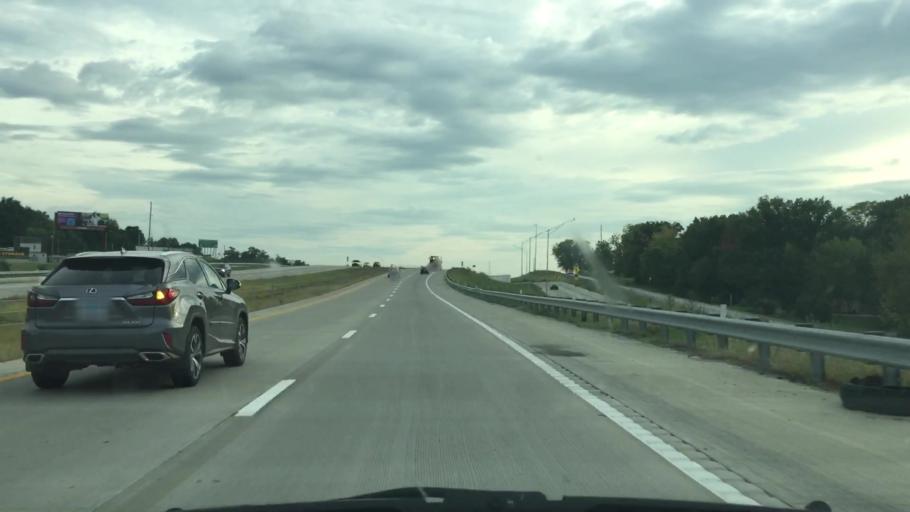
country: US
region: Missouri
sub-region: Clay County
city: Pleasant Valley
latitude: 39.2227
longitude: -94.4711
